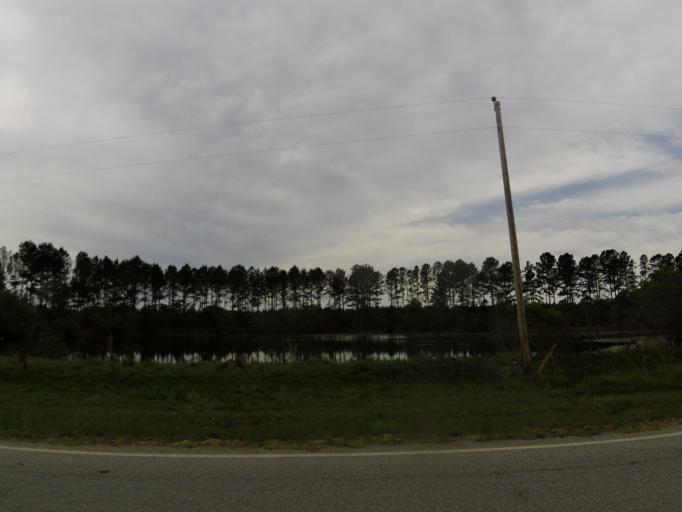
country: US
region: Georgia
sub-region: Emanuel County
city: Twin City
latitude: 32.4659
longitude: -82.2344
